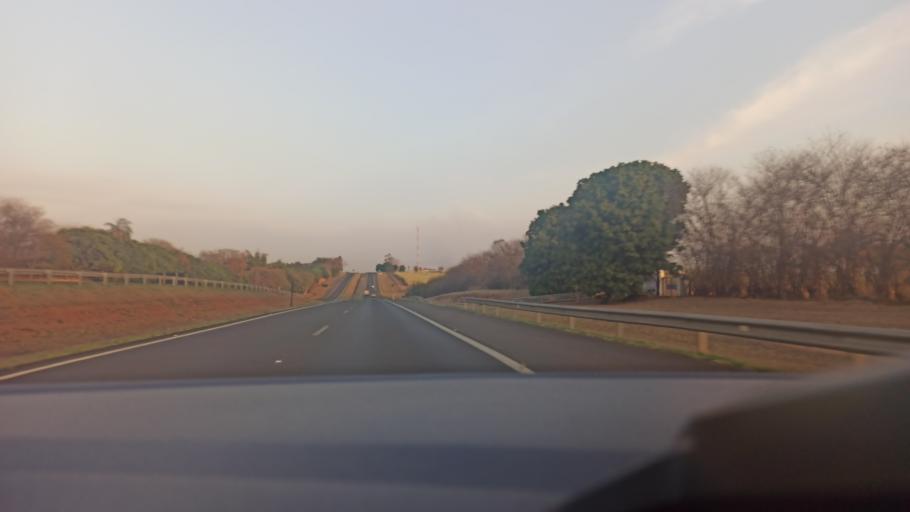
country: BR
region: Sao Paulo
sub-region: Taquaritinga
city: Taquaritinga
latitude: -21.4083
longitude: -48.6957
